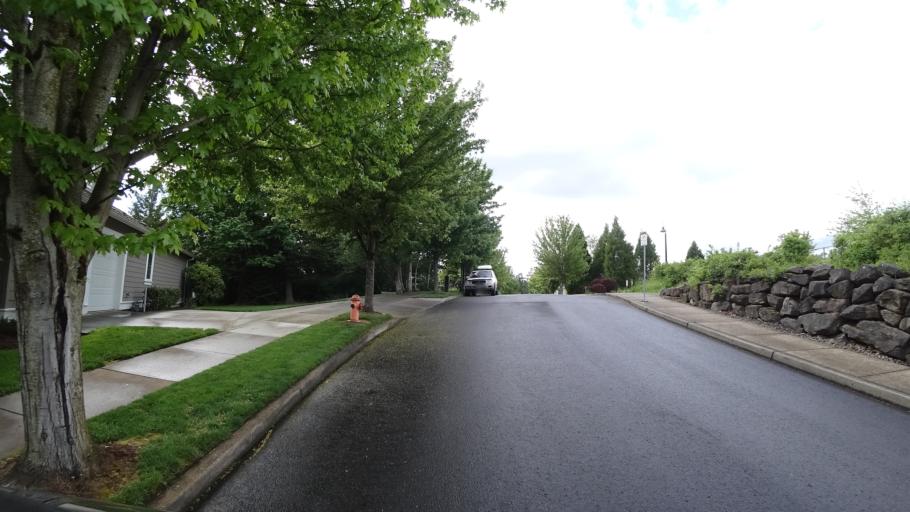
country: US
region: Oregon
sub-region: Washington County
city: West Haven
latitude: 45.5418
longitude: -122.7782
